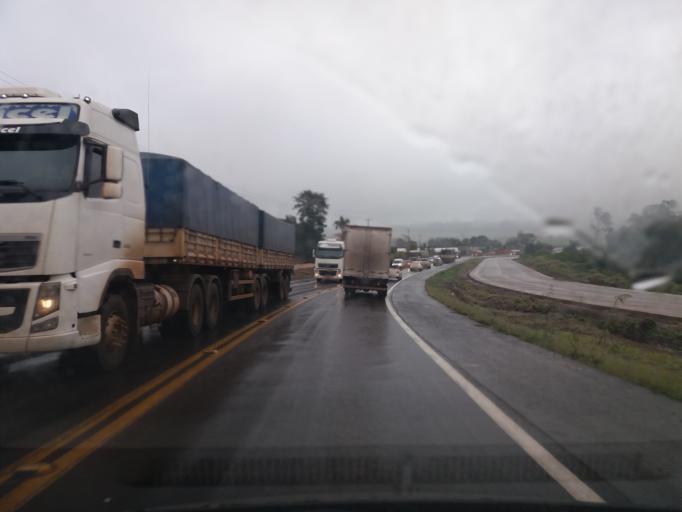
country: BR
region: Parana
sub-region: Realeza
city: Realeza
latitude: -25.4531
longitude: -53.5819
